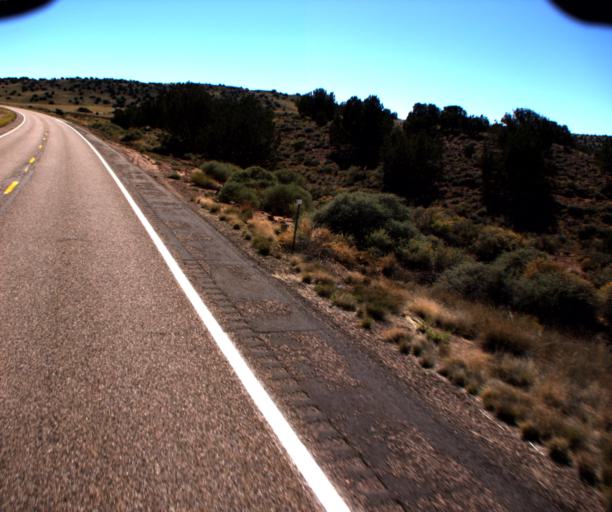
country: US
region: Arizona
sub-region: Apache County
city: Saint Johns
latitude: 34.5726
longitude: -109.5259
